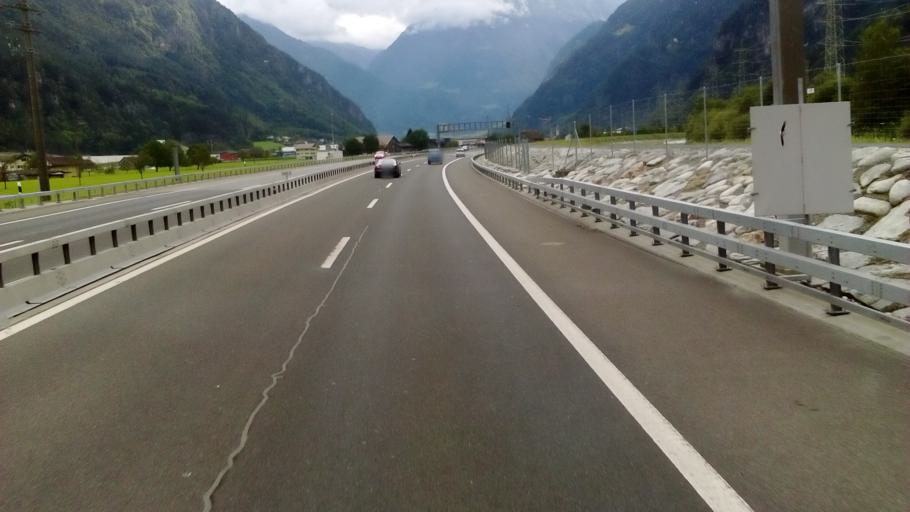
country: CH
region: Uri
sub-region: Uri
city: Attinghausen
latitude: 46.8427
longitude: 8.6354
